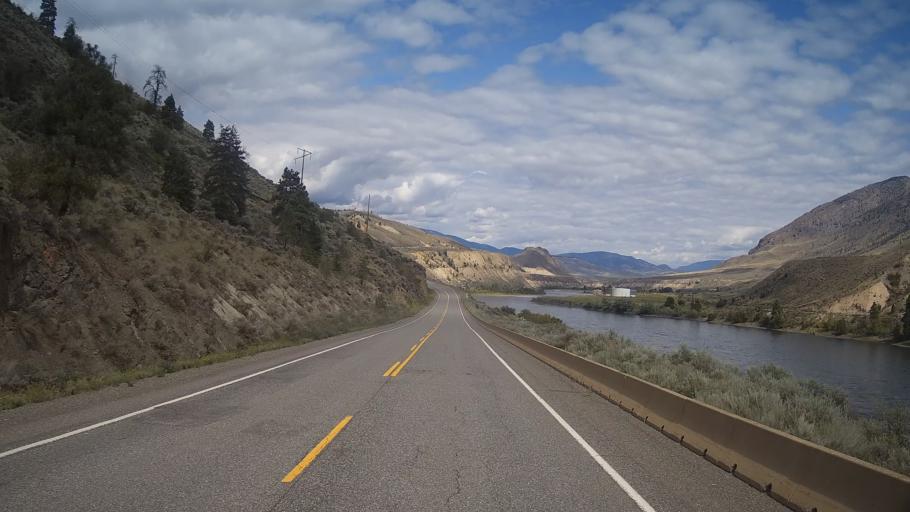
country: CA
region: British Columbia
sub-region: Thompson-Nicola Regional District
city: Ashcroft
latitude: 50.5464
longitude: -121.2924
